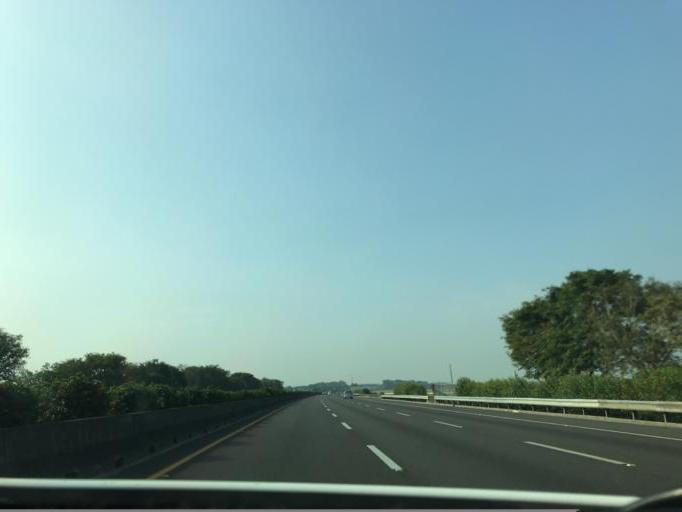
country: TW
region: Taiwan
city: Xinying
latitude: 23.3697
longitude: 120.3488
